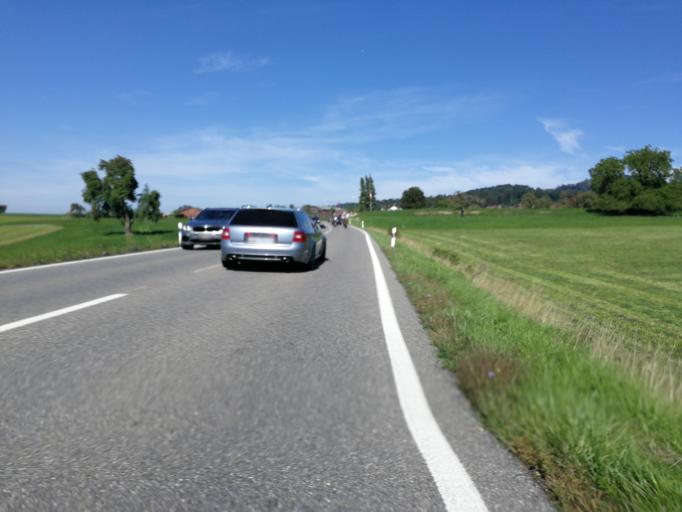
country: CH
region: Zurich
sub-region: Bezirk Hinwil
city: Wetzikon / Kempten
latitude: 47.3186
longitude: 8.8261
